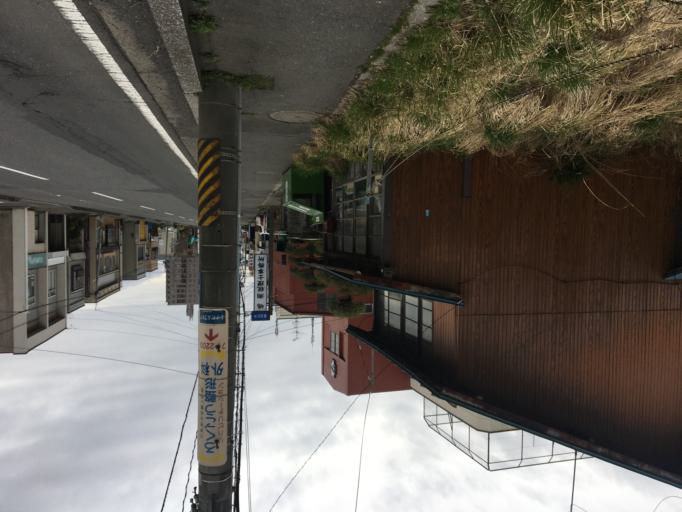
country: JP
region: Aomori
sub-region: Hachinohe Shi
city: Uchimaru
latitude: 40.5219
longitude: 141.5154
